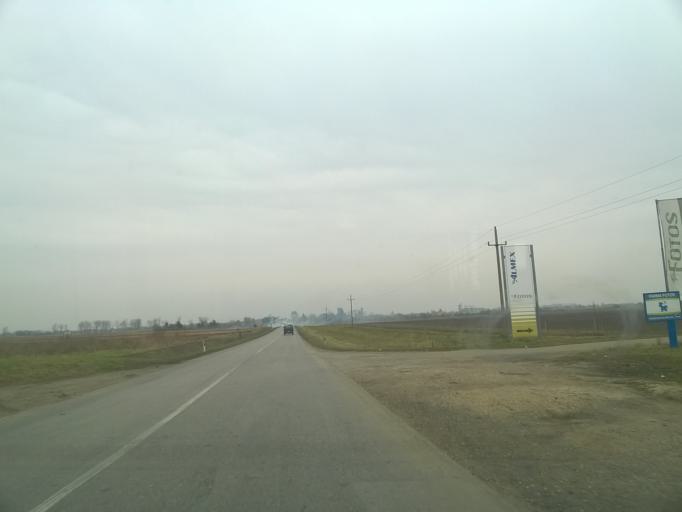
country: RS
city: Crepaja
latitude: 44.9908
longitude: 20.6427
